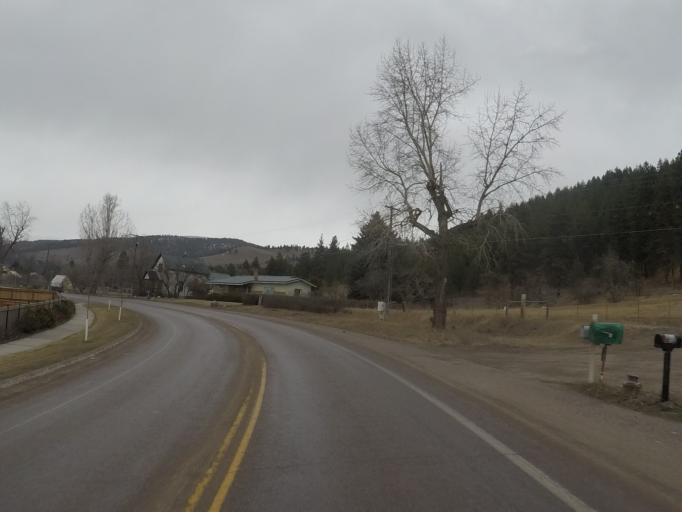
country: US
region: Montana
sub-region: Missoula County
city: East Missoula
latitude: 46.8842
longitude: -113.9662
